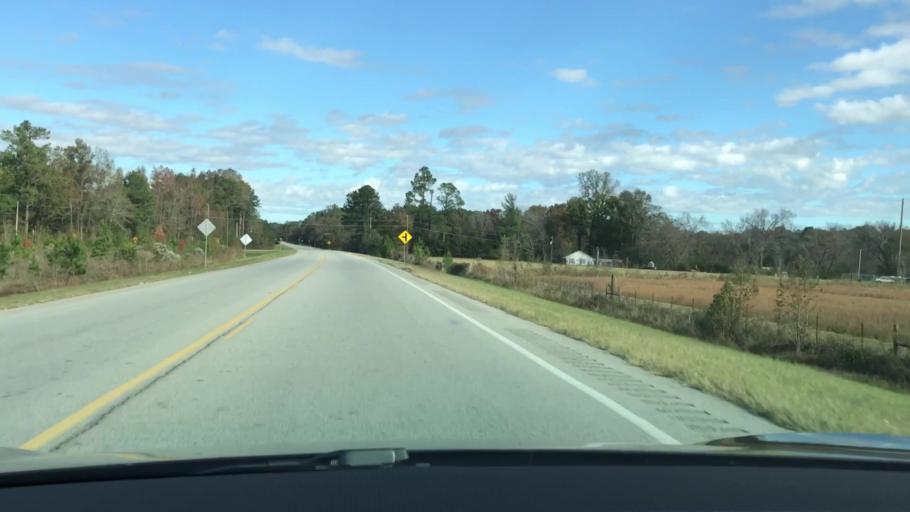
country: US
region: Georgia
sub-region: Jefferson County
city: Louisville
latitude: 32.9631
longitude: -82.3908
